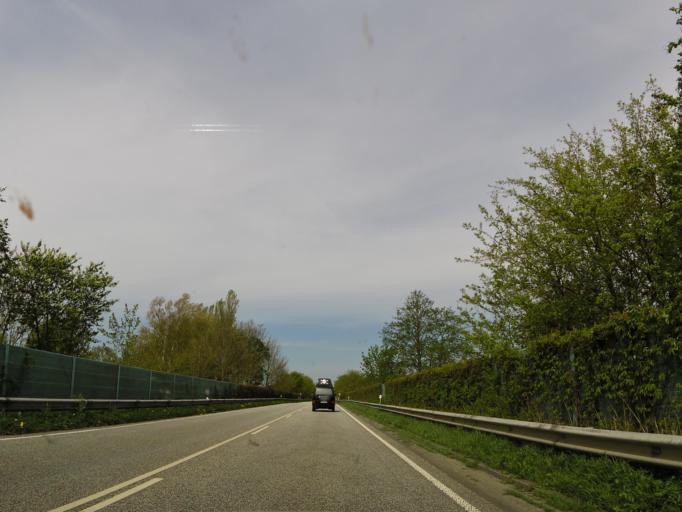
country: DE
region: Schleswig-Holstein
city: Groven
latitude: 54.2916
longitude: 8.9805
